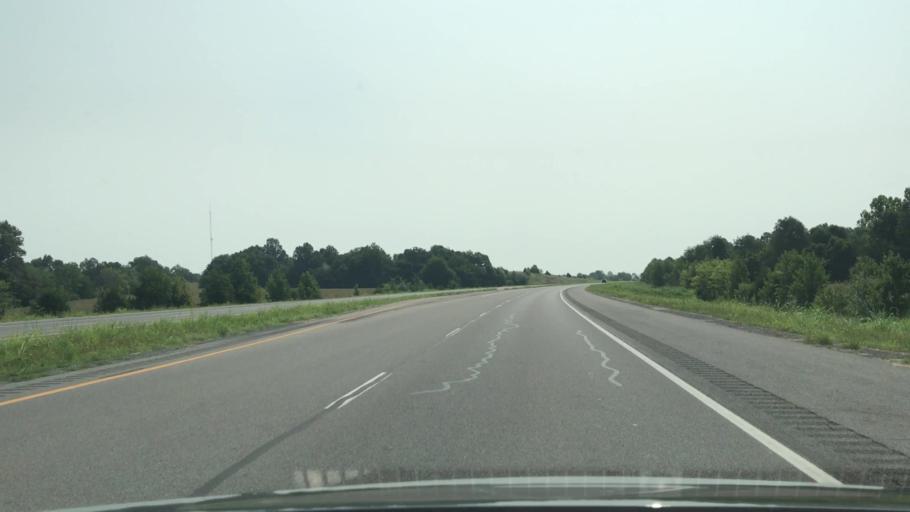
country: US
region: Kentucky
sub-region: Graves County
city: Mayfield
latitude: 36.6918
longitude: -88.5563
